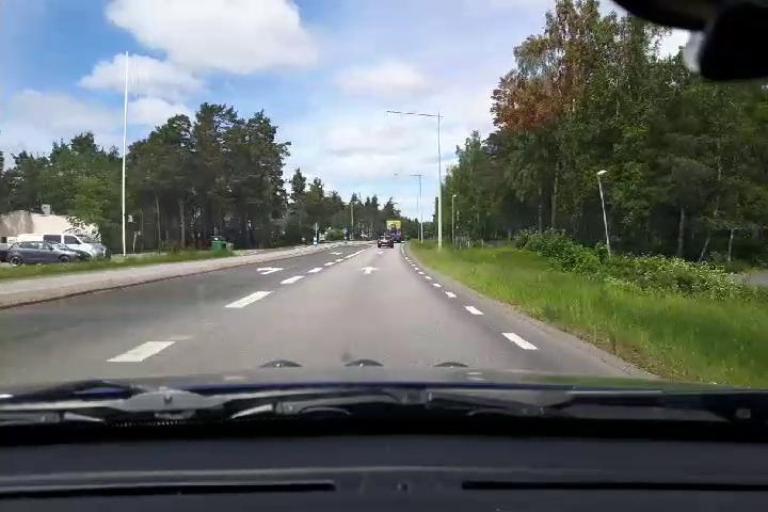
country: SE
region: Uppsala
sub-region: Osthammars Kommun
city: Bjorklinge
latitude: 60.0303
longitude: 17.5526
